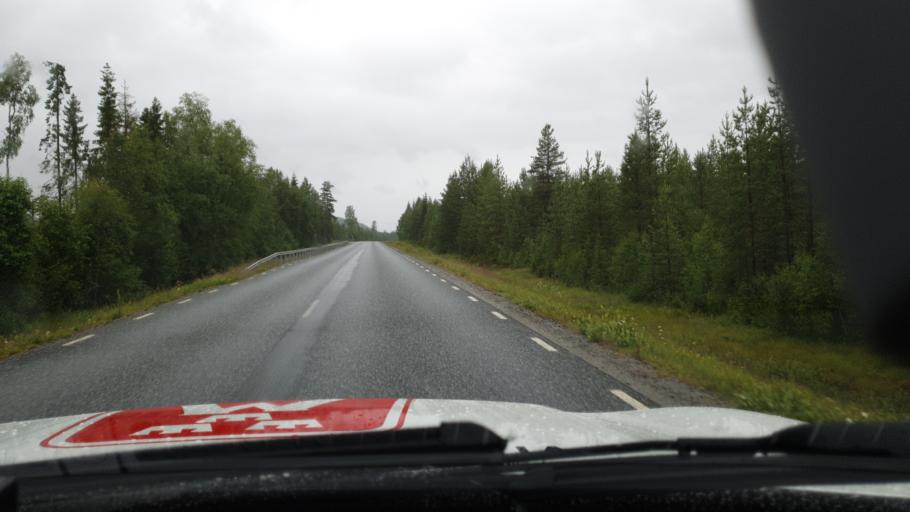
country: SE
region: Vaesterbotten
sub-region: Vilhelmina Kommun
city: Vilhelmina
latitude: 64.4015
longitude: 16.8438
